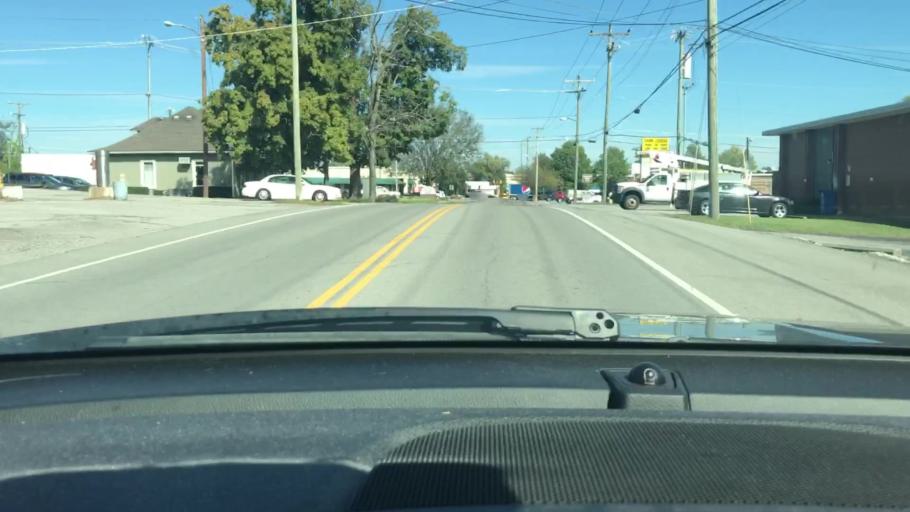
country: US
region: Tennessee
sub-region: Sumner County
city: Hendersonville
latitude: 36.3023
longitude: -86.6203
